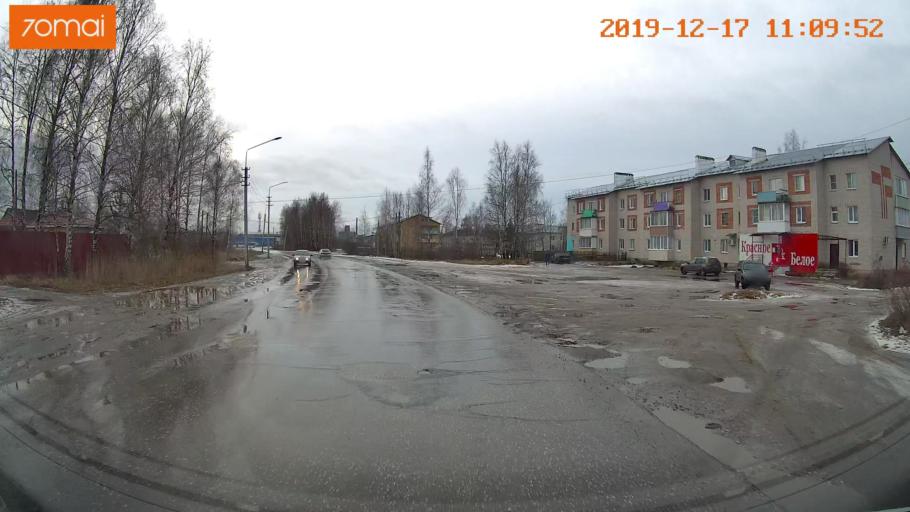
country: RU
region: Vladimir
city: Gus'-Khrustal'nyy
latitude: 55.5970
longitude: 40.6414
